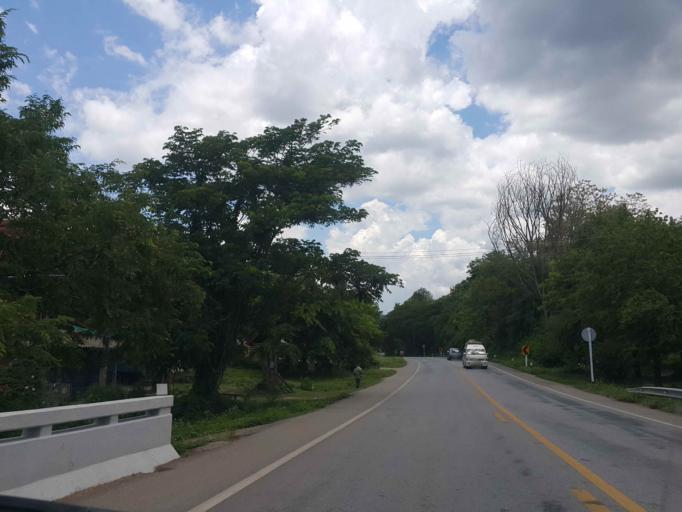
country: TH
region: Nan
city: Wiang Sa
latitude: 18.5227
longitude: 100.5634
